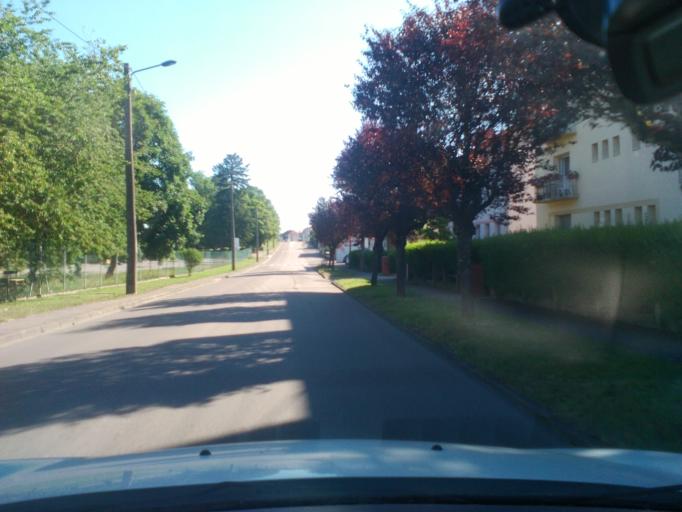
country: FR
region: Lorraine
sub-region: Departement des Vosges
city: Mirecourt
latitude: 48.2922
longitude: 6.1307
